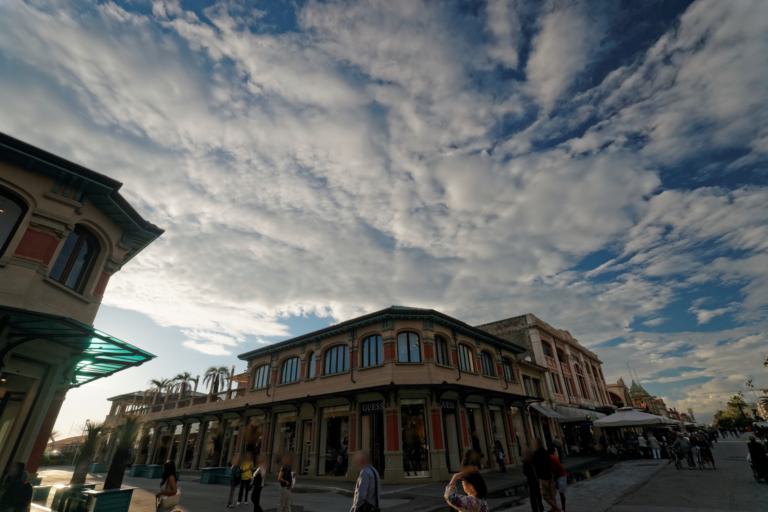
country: IT
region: Tuscany
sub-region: Provincia di Lucca
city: Viareggio
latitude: 43.8664
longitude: 10.2437
